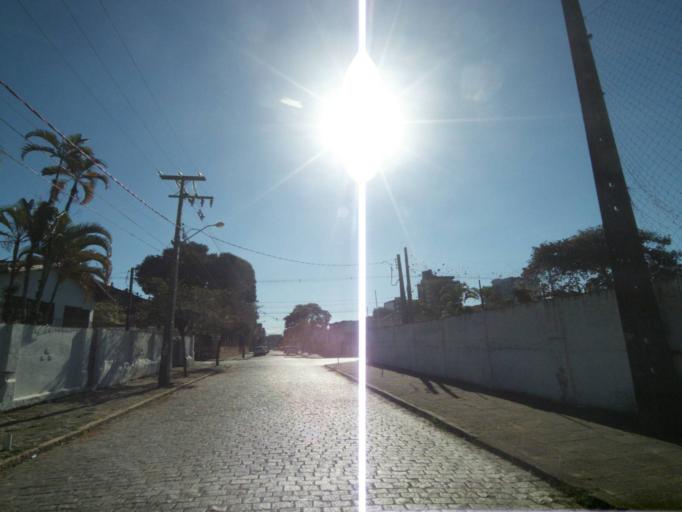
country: BR
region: Parana
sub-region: Paranagua
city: Paranagua
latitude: -25.5168
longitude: -48.5027
